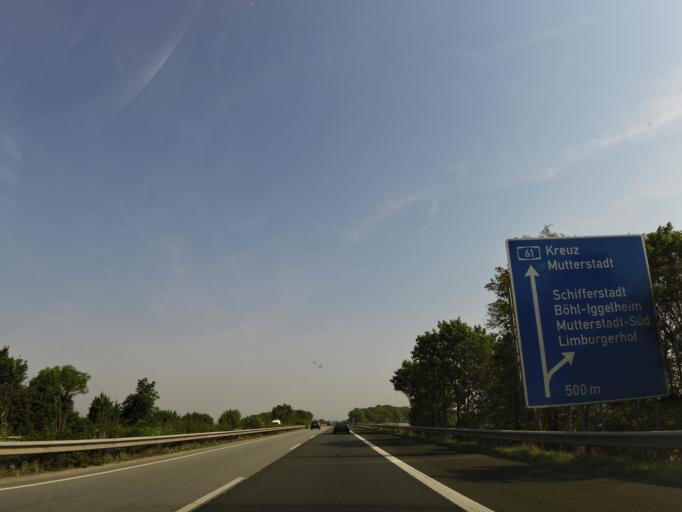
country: DE
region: Rheinland-Pfalz
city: Schifferstadt
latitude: 49.3857
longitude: 8.3408
